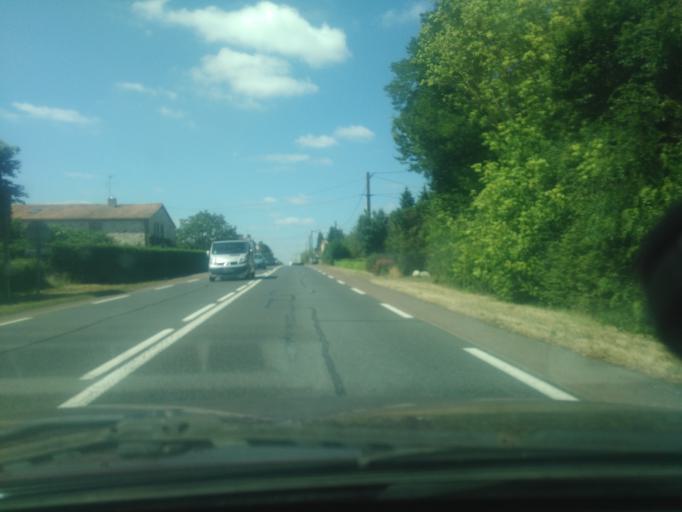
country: FR
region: Pays de la Loire
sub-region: Departement de la Vendee
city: Les Essarts
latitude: 46.7567
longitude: -1.2505
